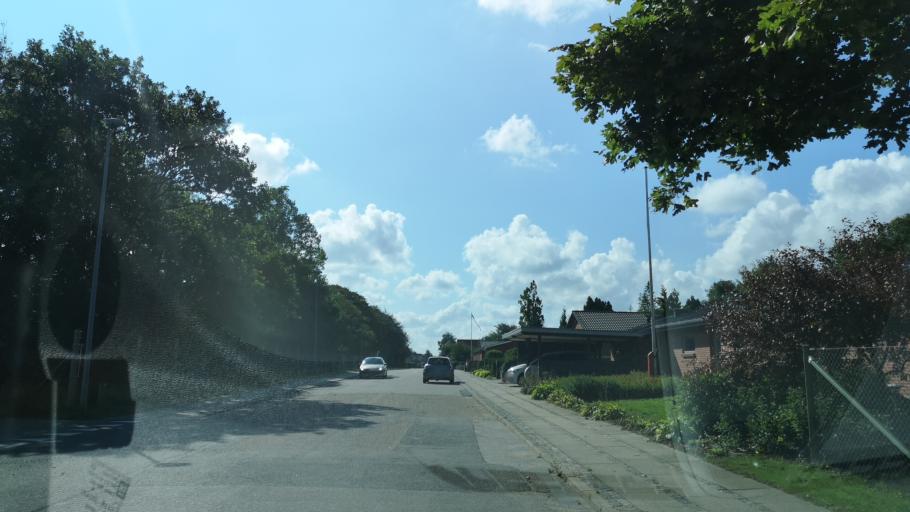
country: DK
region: Central Jutland
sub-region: Ringkobing-Skjern Kommune
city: Skjern
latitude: 55.9547
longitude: 8.4974
